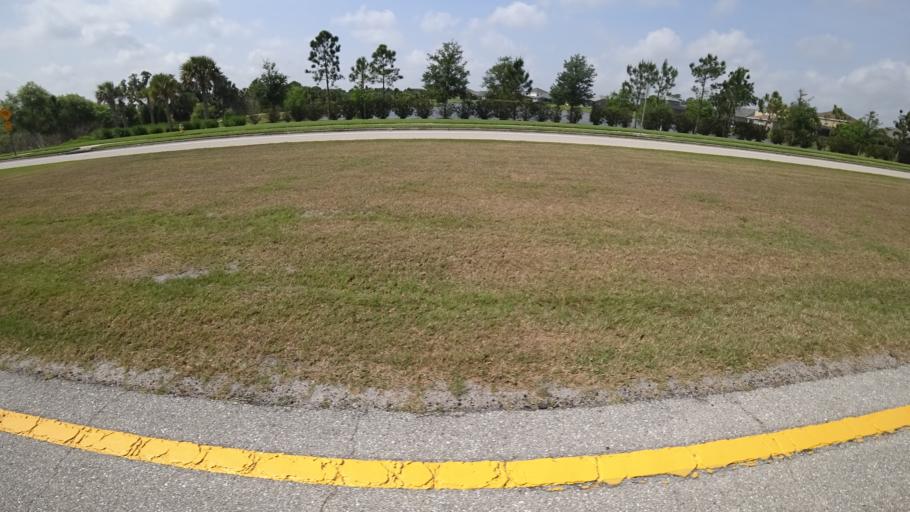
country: US
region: Florida
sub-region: Sarasota County
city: North Sarasota
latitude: 27.4184
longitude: -82.5106
